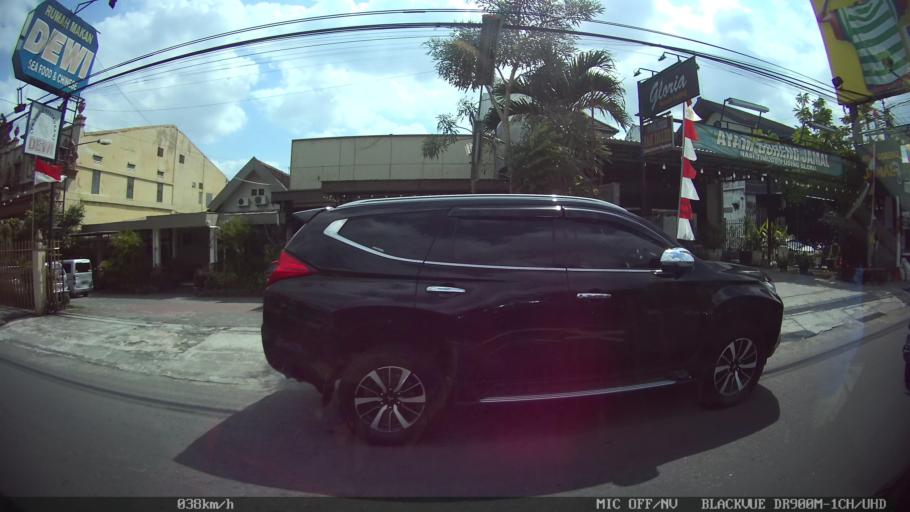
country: ID
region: Daerah Istimewa Yogyakarta
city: Yogyakarta
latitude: -7.7666
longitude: 110.3611
